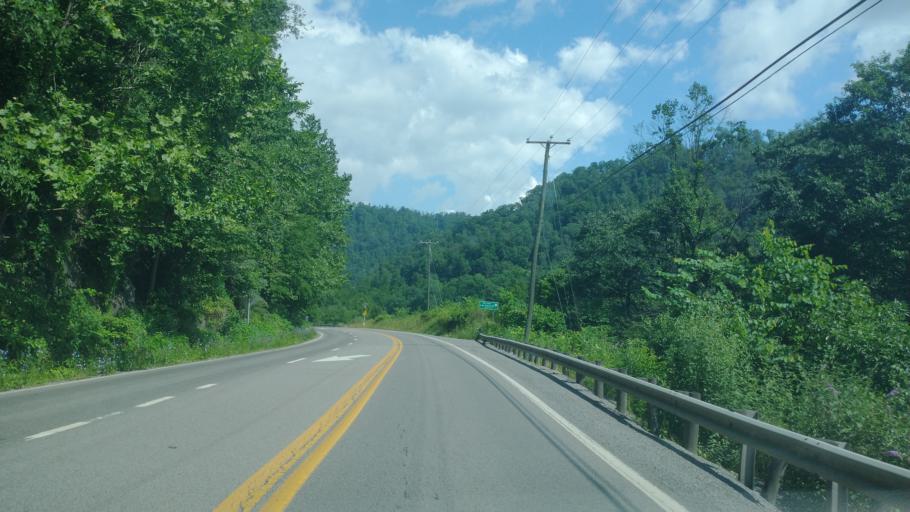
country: US
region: West Virginia
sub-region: McDowell County
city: Welch
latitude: 37.4212
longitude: -81.5451
